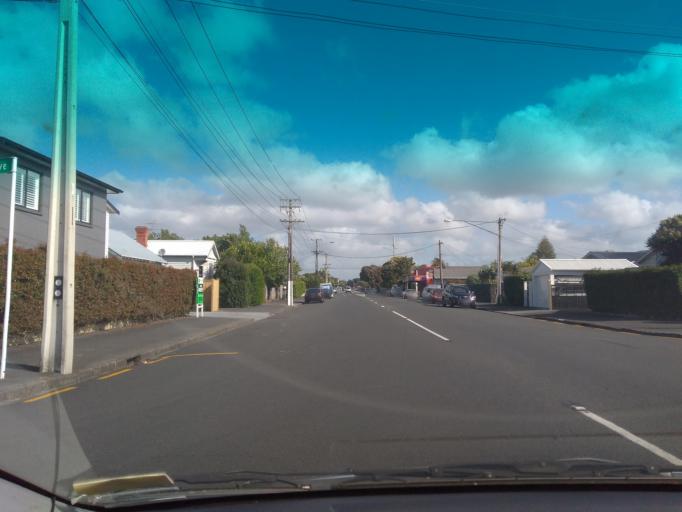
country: NZ
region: Auckland
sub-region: Auckland
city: Rosebank
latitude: -36.8627
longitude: 174.7044
